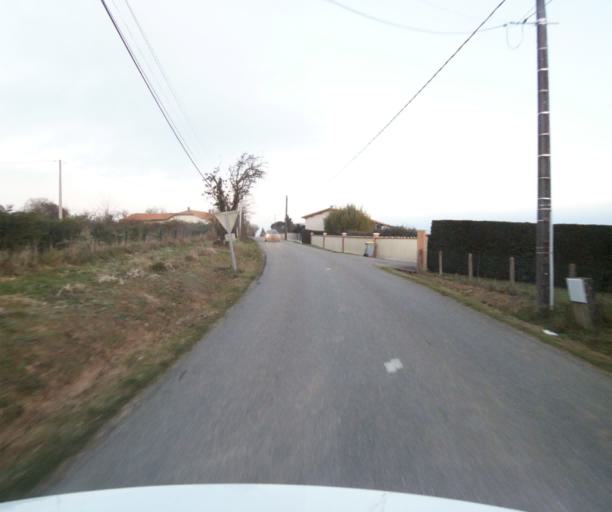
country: FR
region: Midi-Pyrenees
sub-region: Departement du Tarn-et-Garonne
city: Moissac
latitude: 44.1219
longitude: 1.0745
